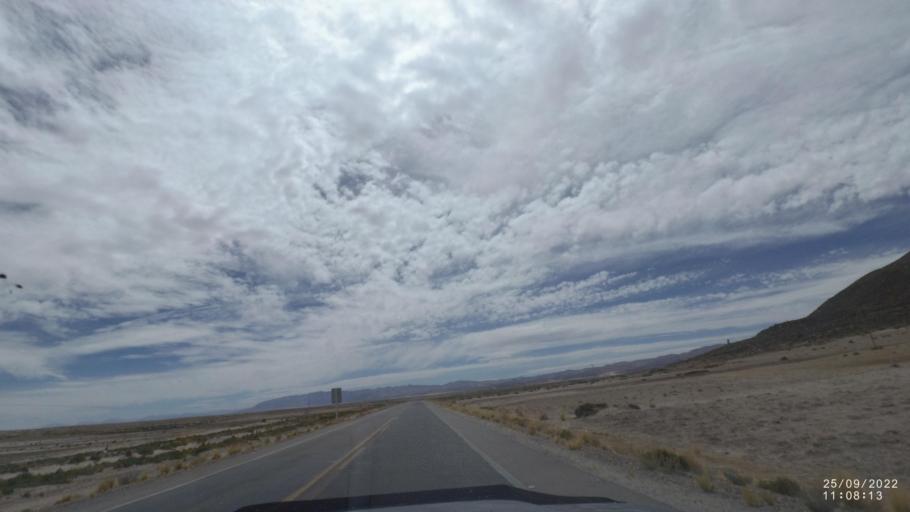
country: BO
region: Oruro
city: Challapata
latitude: -19.3309
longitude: -66.8508
